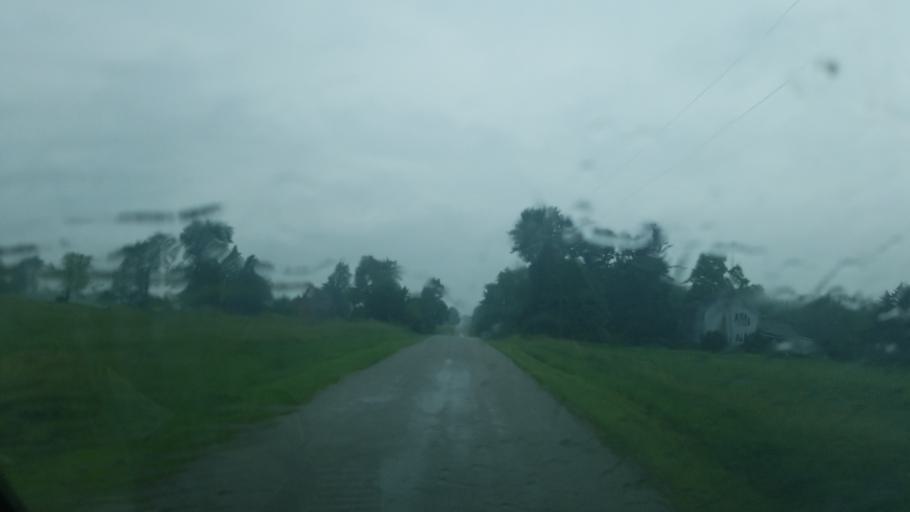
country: US
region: Ohio
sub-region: Richland County
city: Shelby
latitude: 40.9259
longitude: -82.7976
